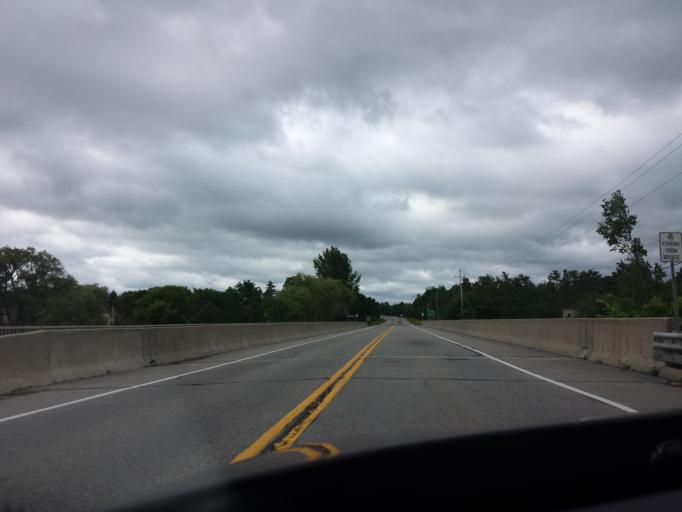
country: CA
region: Ontario
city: Carleton Place
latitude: 45.0533
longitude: -76.2507
